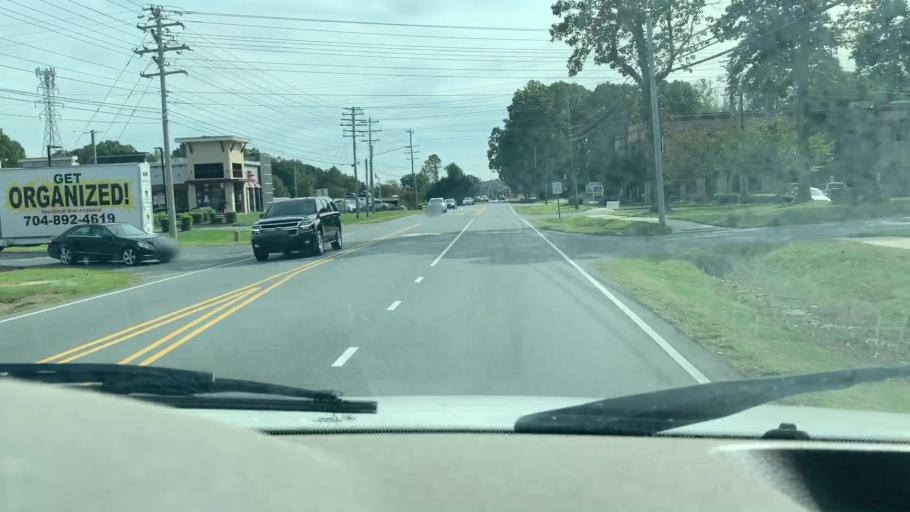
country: US
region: North Carolina
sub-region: Mecklenburg County
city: Cornelius
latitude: 35.4746
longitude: -80.8916
